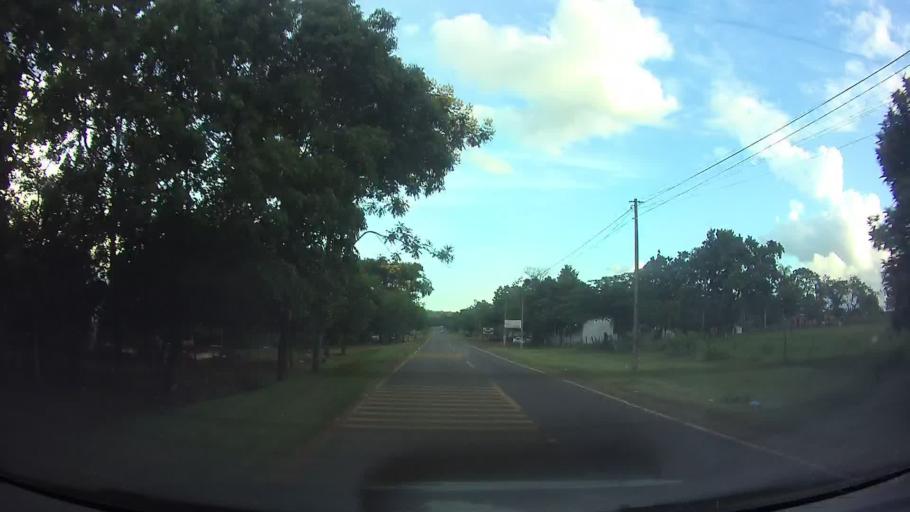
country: PY
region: Paraguari
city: Acahay
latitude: -25.9187
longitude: -57.1108
